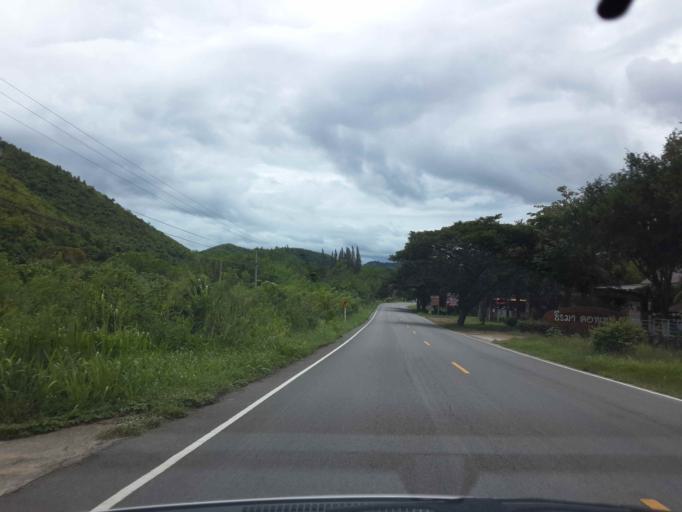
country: TH
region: Ratchaburi
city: Suan Phueng
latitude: 13.5579
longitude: 99.2721
